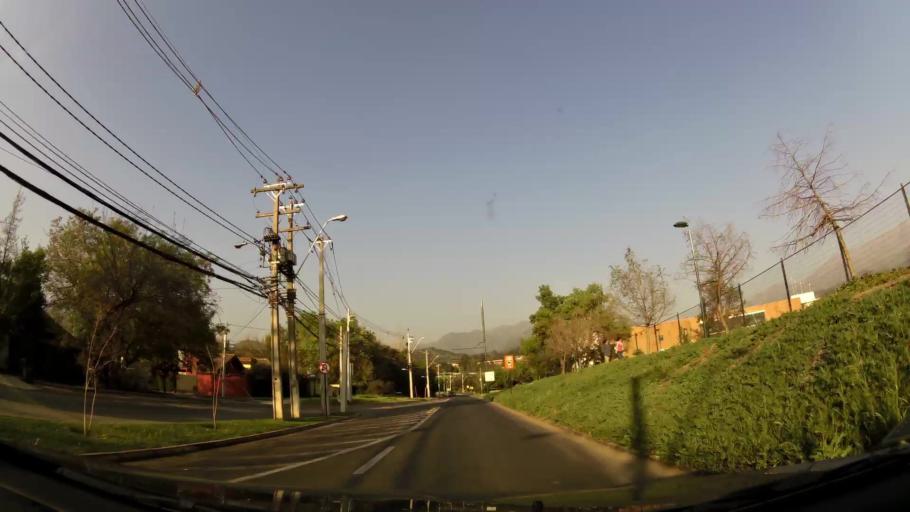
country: CL
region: Santiago Metropolitan
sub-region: Provincia de Santiago
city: Villa Presidente Frei, Nunoa, Santiago, Chile
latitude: -33.3513
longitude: -70.5091
